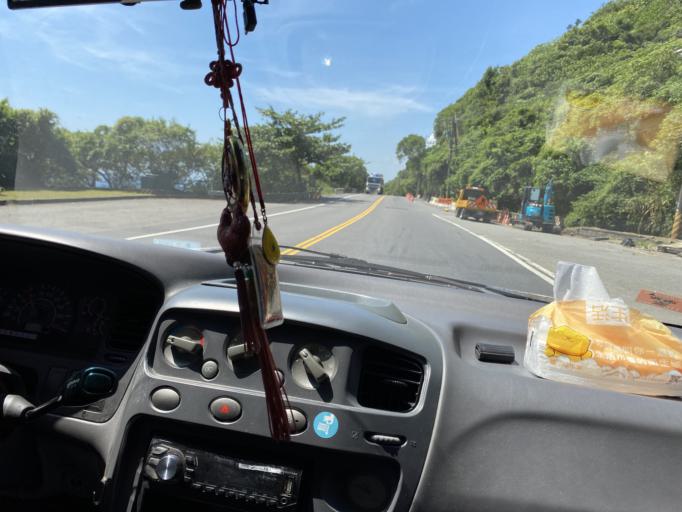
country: TW
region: Taiwan
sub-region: Keelung
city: Keelung
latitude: 24.9841
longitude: 121.9552
